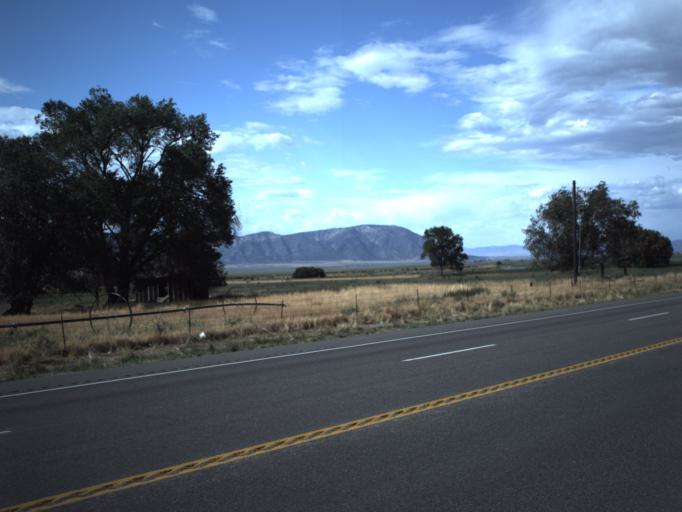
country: US
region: Utah
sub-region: Sanpete County
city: Manti
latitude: 39.2836
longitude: -111.6285
